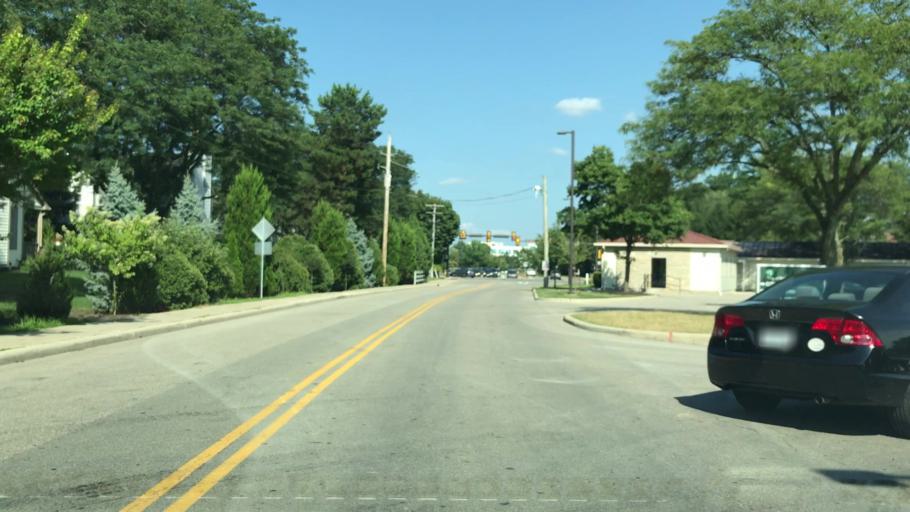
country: US
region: Ohio
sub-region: Franklin County
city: Dublin
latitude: 40.1051
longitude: -83.1346
